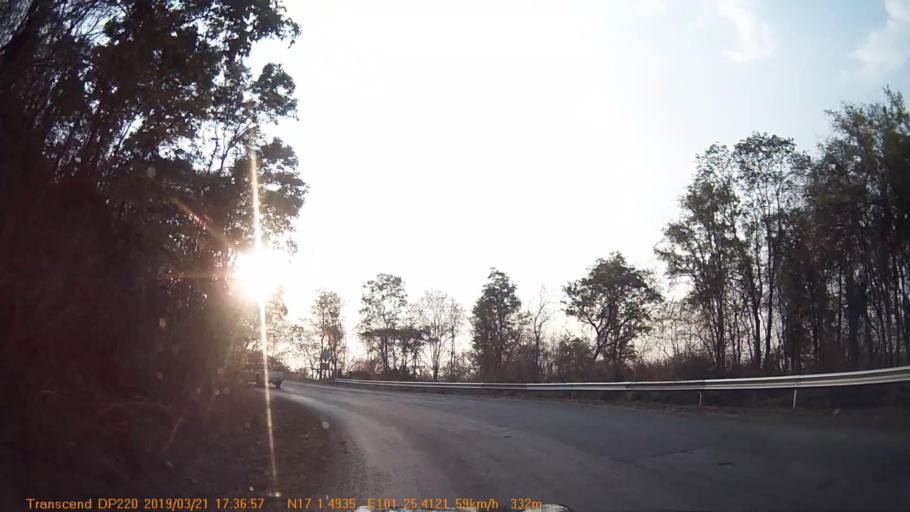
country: TH
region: Phetchabun
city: Lom Kao
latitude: 17.0249
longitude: 101.4234
